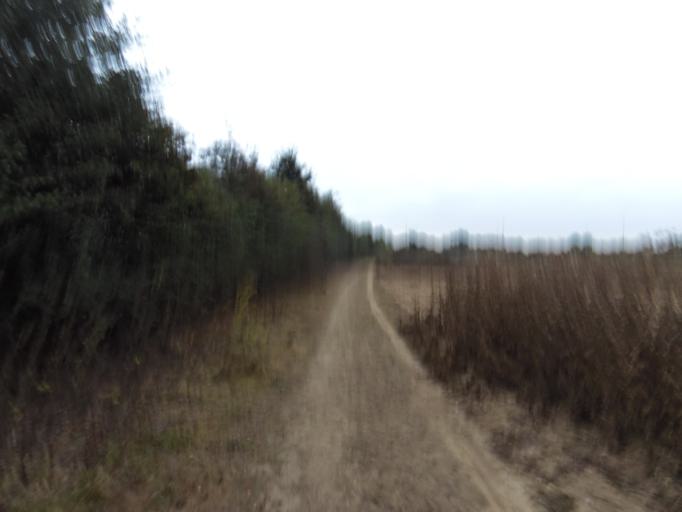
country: GB
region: England
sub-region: Hertfordshire
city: Radlett
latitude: 51.7133
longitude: -0.3134
